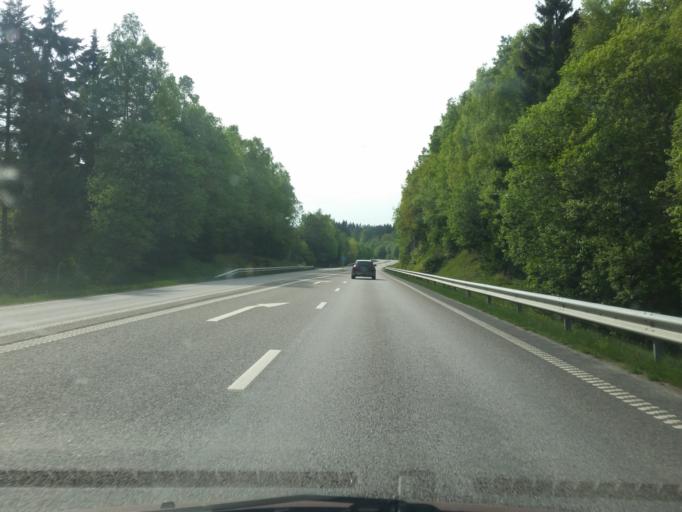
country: SE
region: Vaestra Goetaland
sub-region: Ulricehamns Kommun
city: Ulricehamn
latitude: 57.8038
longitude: 13.3319
